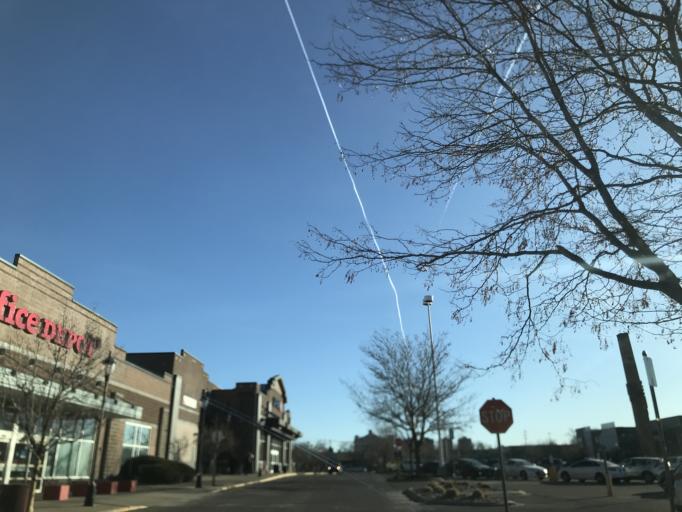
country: US
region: Colorado
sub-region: Denver County
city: Denver
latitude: 39.7102
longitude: -104.9897
